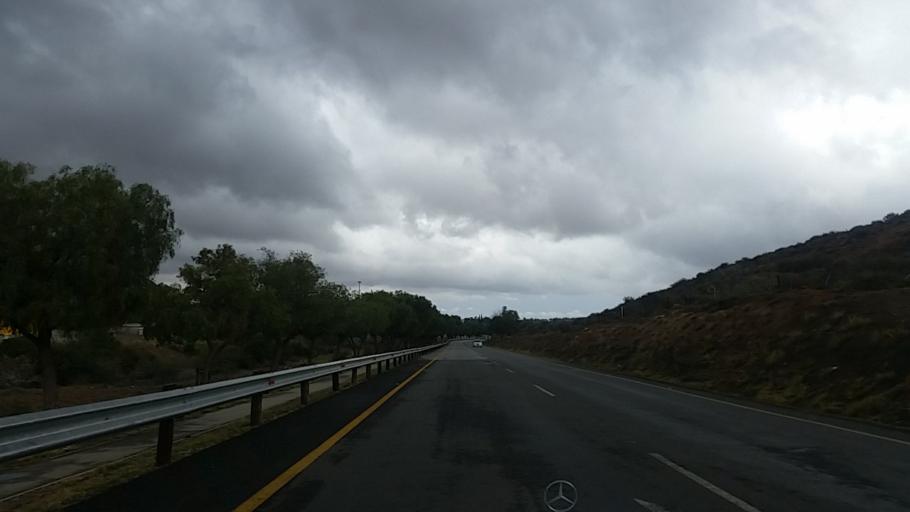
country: ZA
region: Eastern Cape
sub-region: Cacadu District Municipality
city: Graaff-Reinet
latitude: -32.2419
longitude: 24.5371
